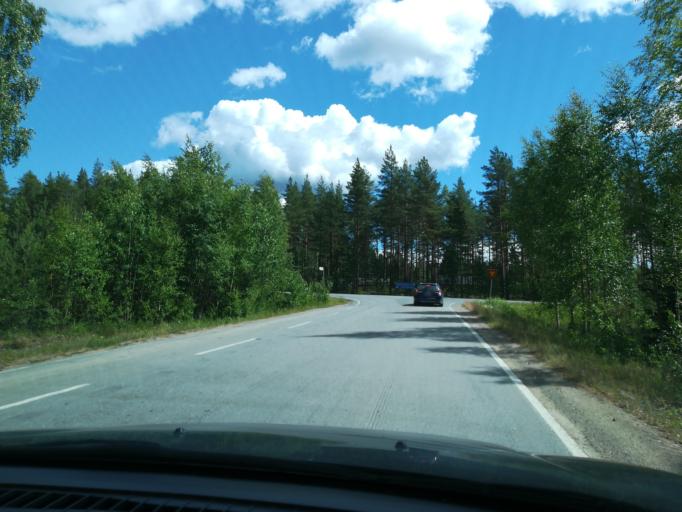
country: FI
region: Southern Savonia
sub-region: Mikkeli
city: Hirvensalmi
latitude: 61.6199
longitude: 26.7804
